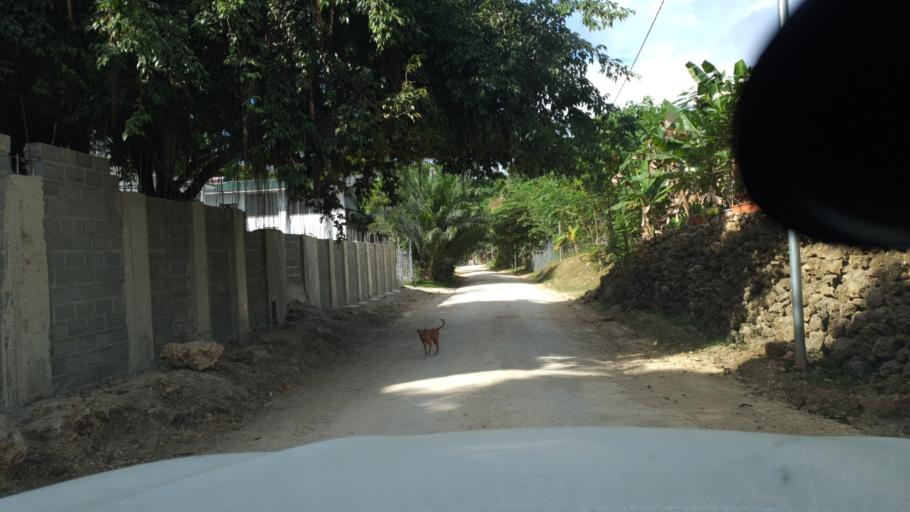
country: SB
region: Guadalcanal
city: Honiara
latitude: -9.4352
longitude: 159.9318
